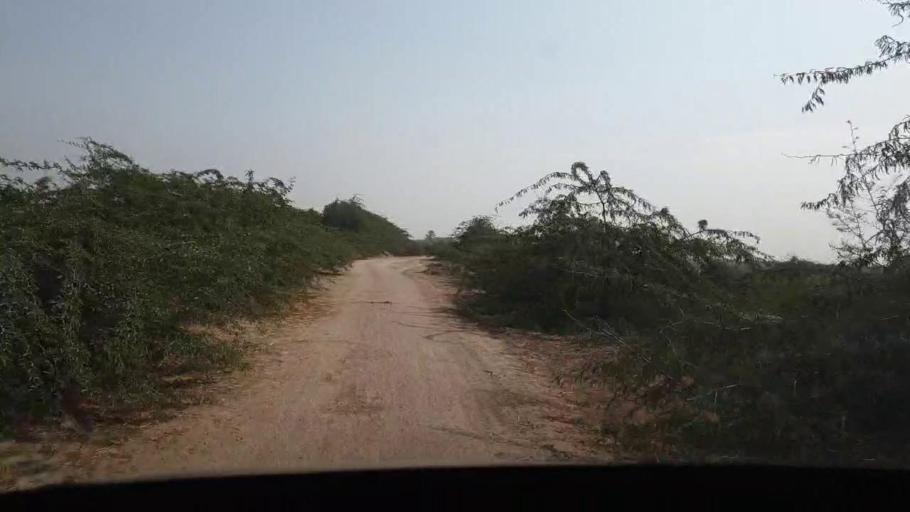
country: PK
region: Sindh
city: Chuhar Jamali
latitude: 24.2543
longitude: 67.9860
